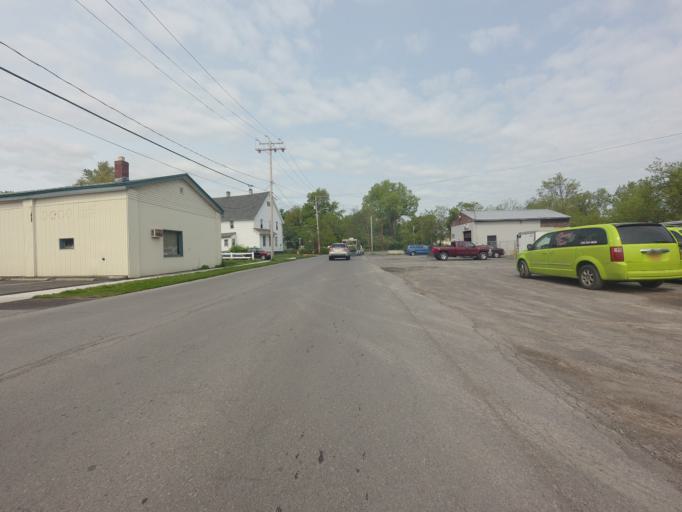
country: US
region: New York
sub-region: Jefferson County
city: Watertown
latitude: 43.9767
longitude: -75.8952
